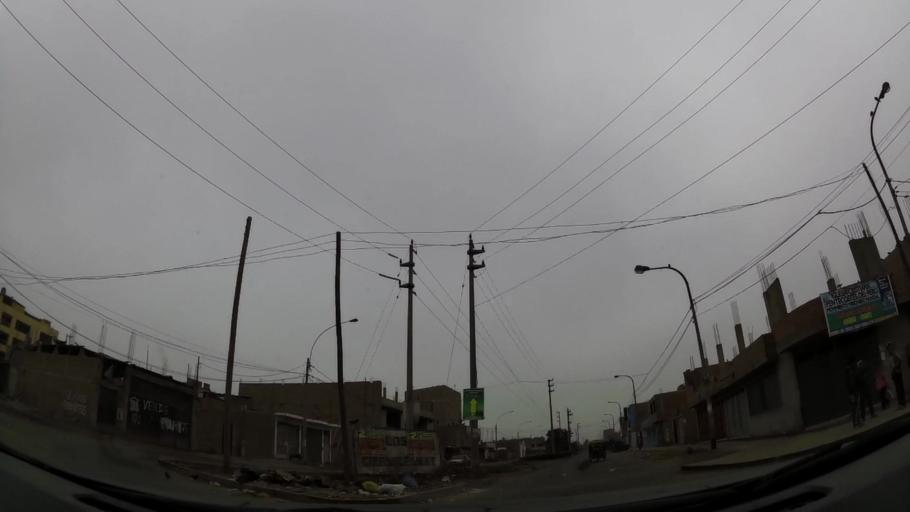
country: PE
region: Lima
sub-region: Lima
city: Urb. Santo Domingo
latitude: -11.8852
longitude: -77.0398
